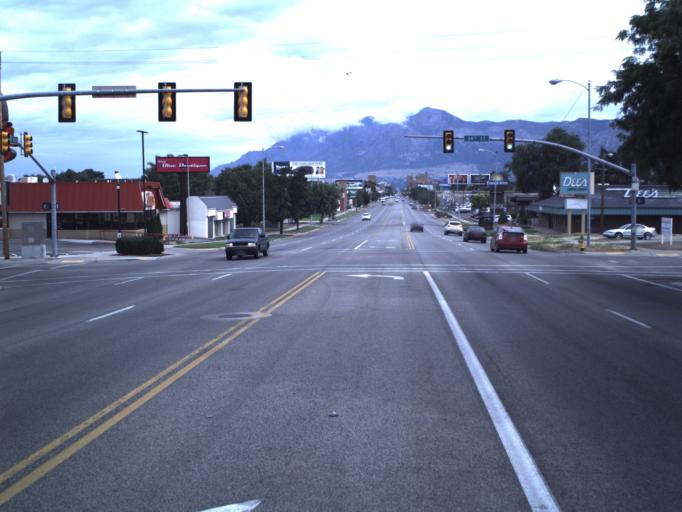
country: US
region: Utah
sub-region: Weber County
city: South Ogden
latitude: 41.2015
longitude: -111.9709
